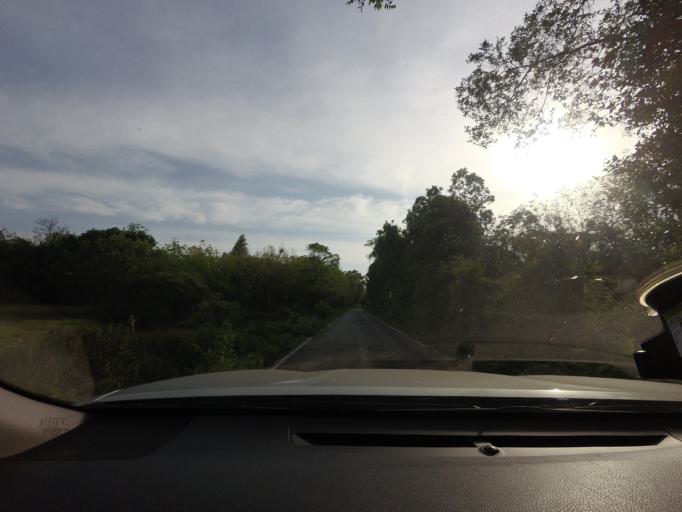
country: TH
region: Narathiwat
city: Ra-ngae
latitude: 6.3029
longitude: 101.7730
